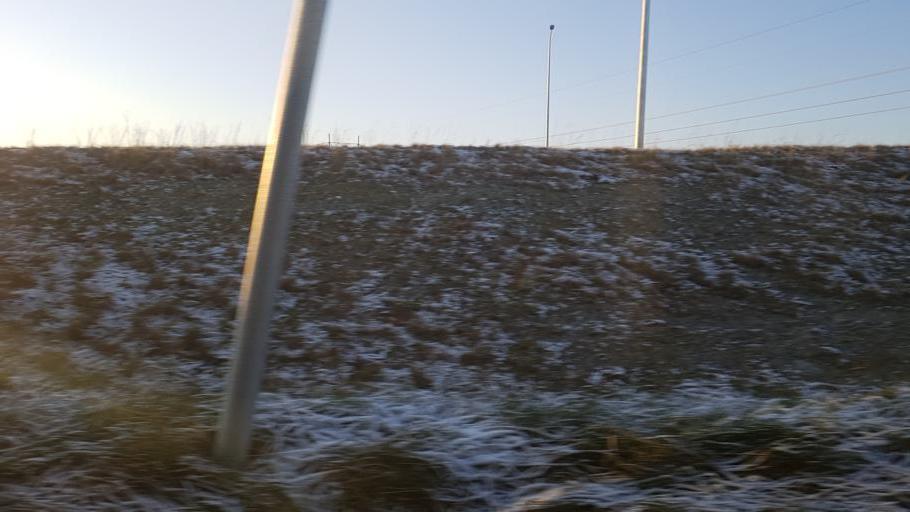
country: NO
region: Sor-Trondelag
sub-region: Melhus
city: Melhus
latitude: 63.3069
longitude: 10.2897
